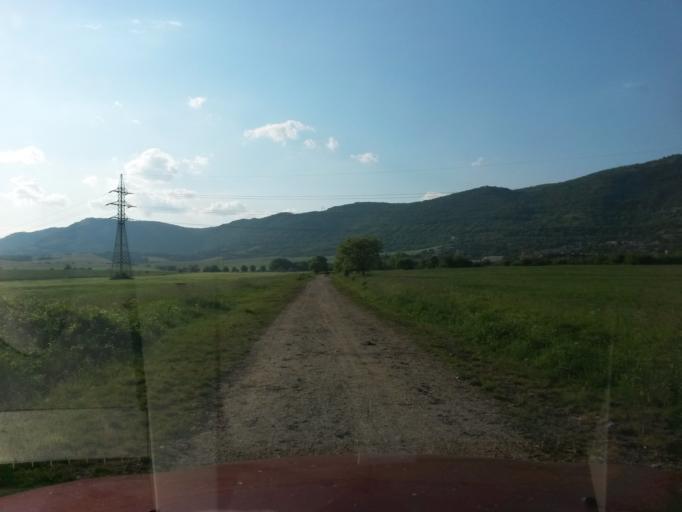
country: SK
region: Kosicky
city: Roznava
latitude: 48.5842
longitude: 20.6779
